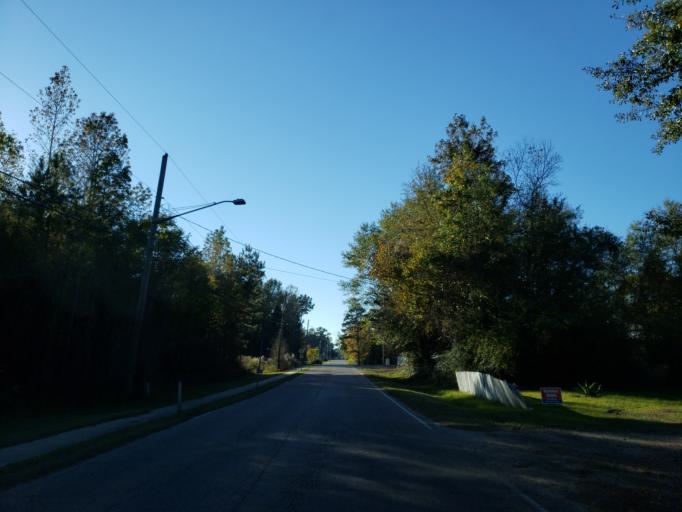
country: US
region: Mississippi
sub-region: Forrest County
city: Hattiesburg
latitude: 31.2774
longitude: -89.2764
